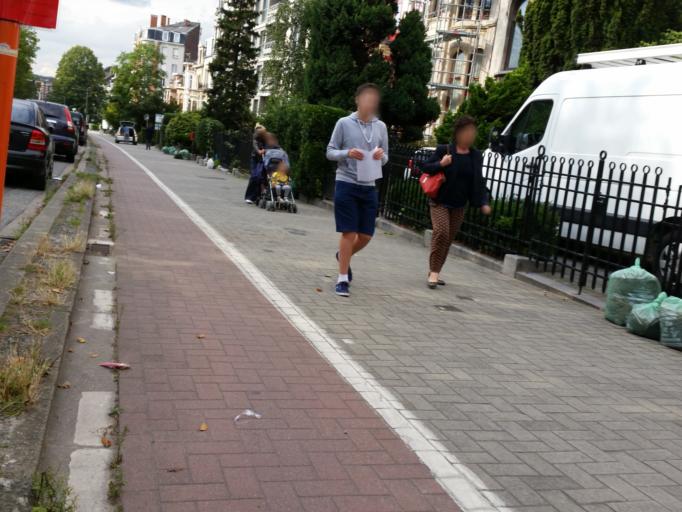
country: BE
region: Brussels Capital
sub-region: Bruxelles-Capitale
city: Brussels
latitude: 50.8716
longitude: 4.3816
